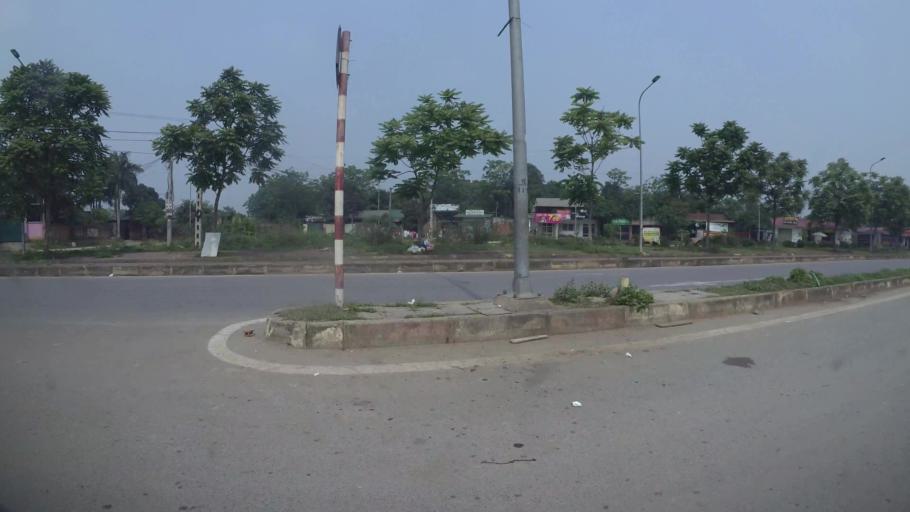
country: VN
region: Ha Noi
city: Lien Quan
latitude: 20.9875
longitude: 105.5364
